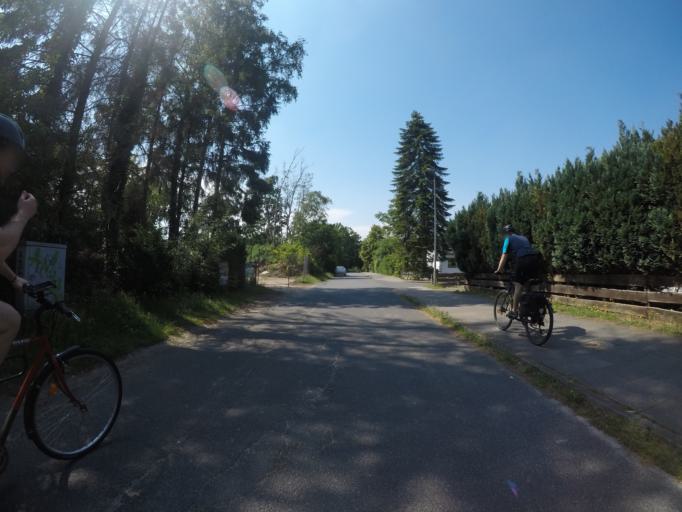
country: DE
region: Lower Saxony
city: Buchholz in der Nordheide
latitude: 53.3259
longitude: 9.8432
